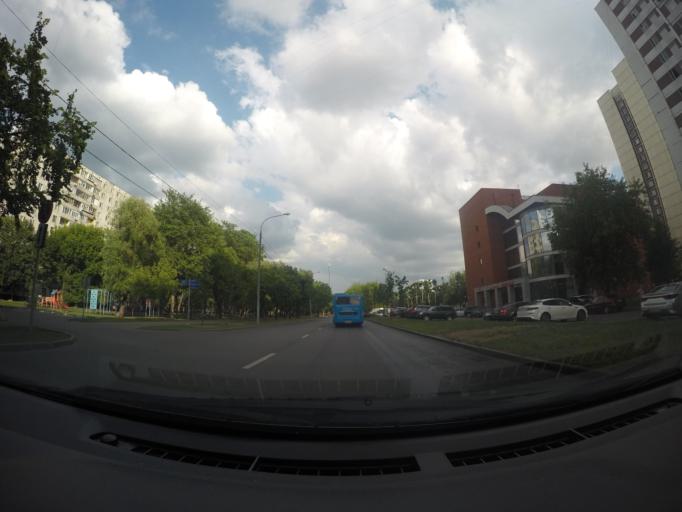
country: RU
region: Moscow
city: Kozeyevo
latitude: 55.8604
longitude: 37.6167
